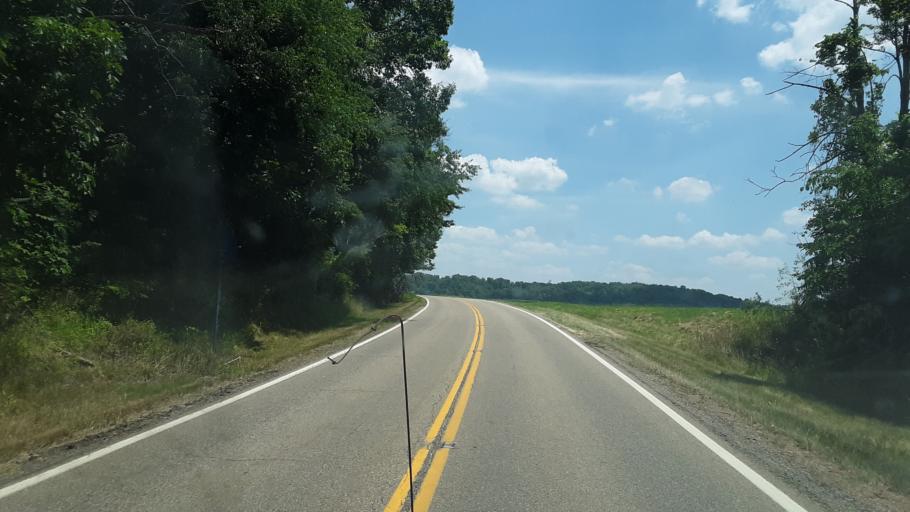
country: US
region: Ohio
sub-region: Tuscarawas County
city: Strasburg
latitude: 40.6540
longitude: -81.4841
